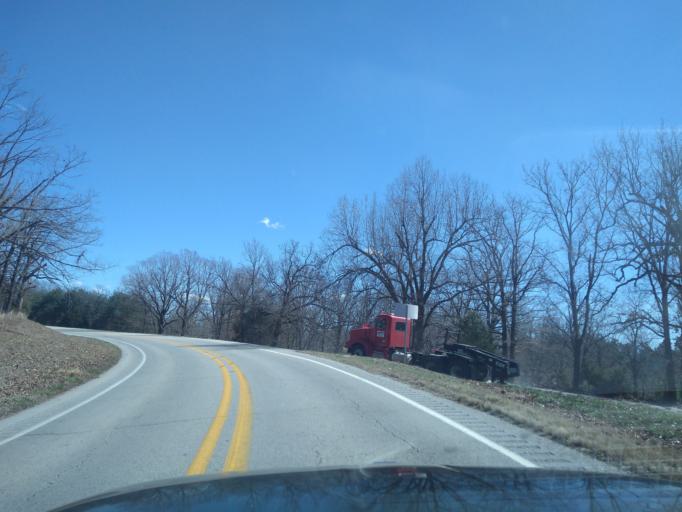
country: US
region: Arkansas
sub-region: Washington County
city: Farmington
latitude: 36.0804
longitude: -94.3190
